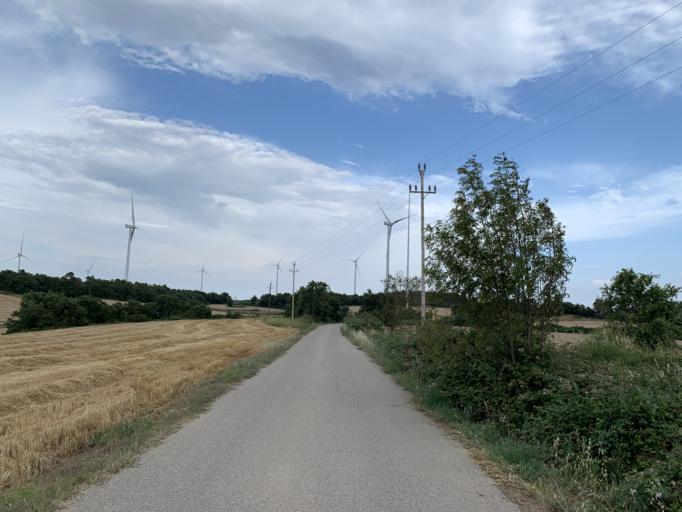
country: ES
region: Catalonia
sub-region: Provincia de Tarragona
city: Conesa
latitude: 41.5415
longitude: 1.2746
